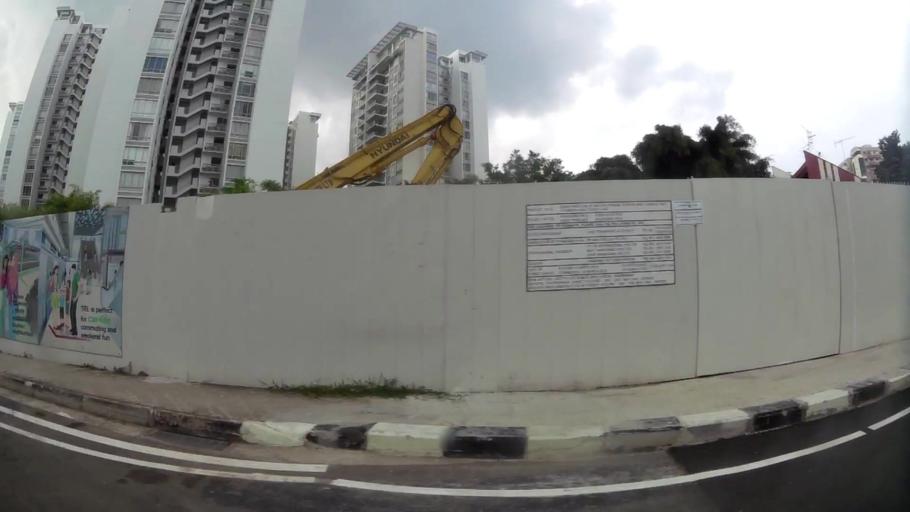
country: SG
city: Singapore
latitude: 1.3018
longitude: 103.9036
